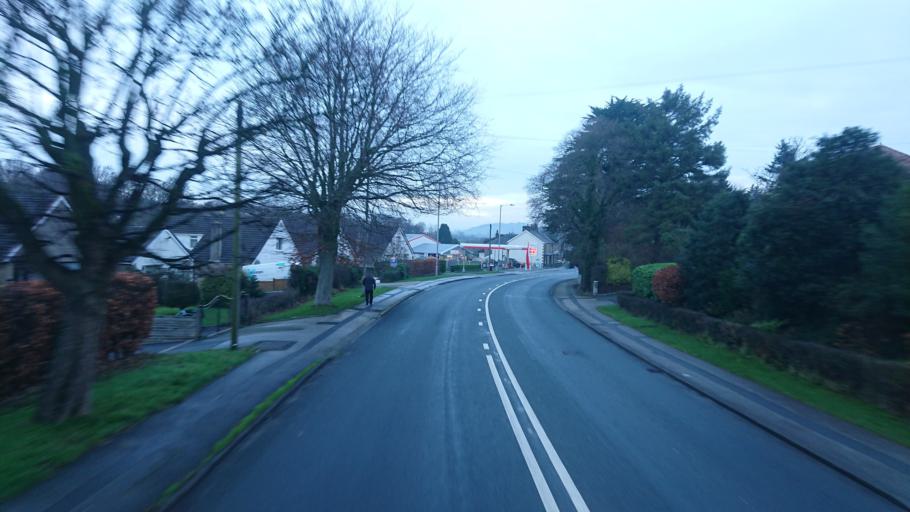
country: GB
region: England
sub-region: Lancashire
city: Bolton le Sands
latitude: 54.0963
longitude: -2.8029
